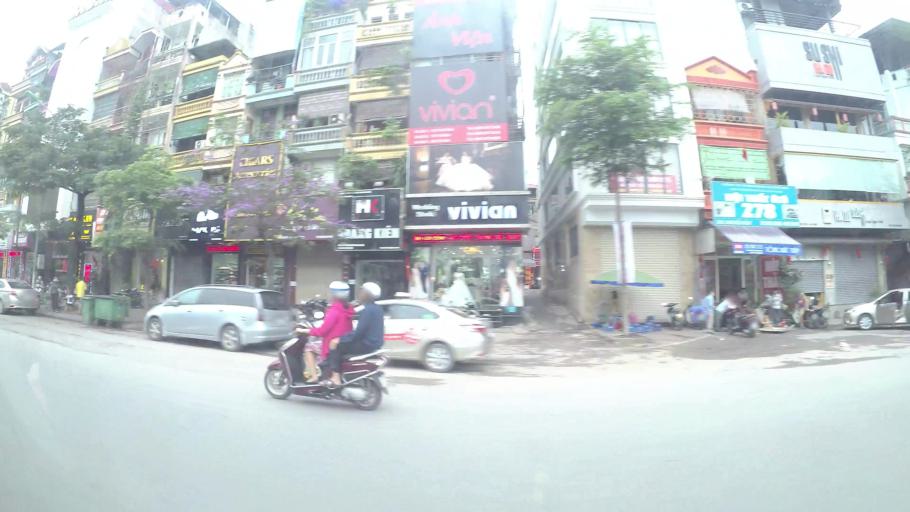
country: VN
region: Ha Noi
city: Dong Da
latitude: 21.0131
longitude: 105.8358
